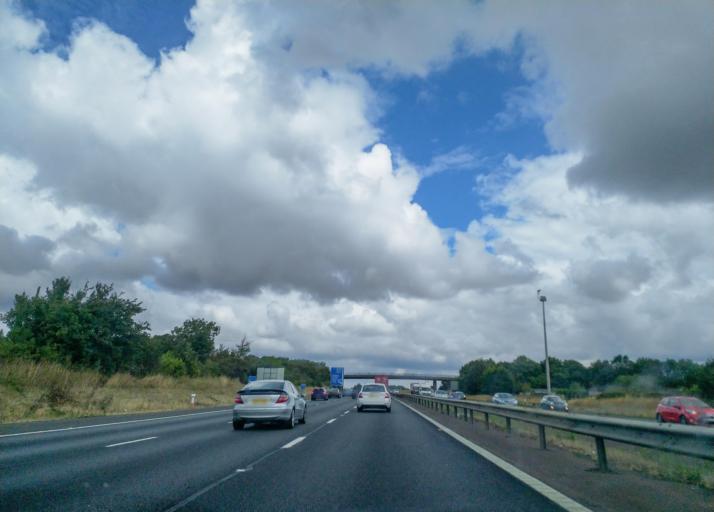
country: GB
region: England
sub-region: Oxfordshire
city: Bicester
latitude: 51.9382
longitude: -1.2018
